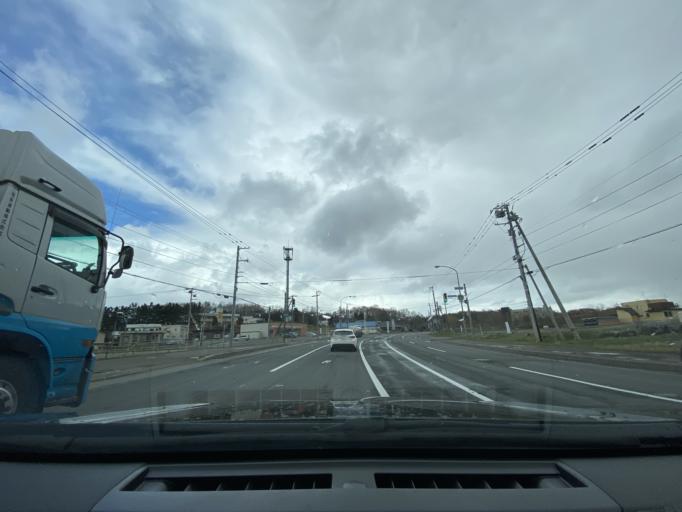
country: JP
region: Hokkaido
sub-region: Asahikawa-shi
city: Asahikawa
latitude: 43.7669
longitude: 142.2820
